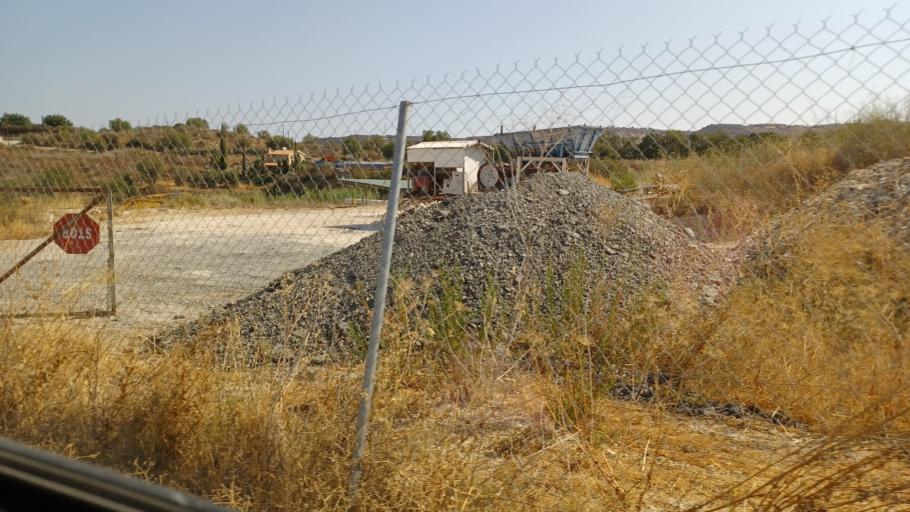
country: CY
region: Pafos
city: Tala
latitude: 34.9105
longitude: 32.4802
